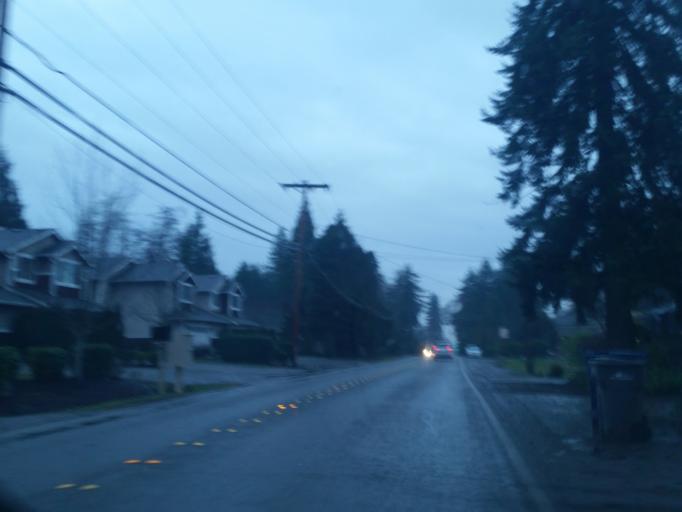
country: US
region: Washington
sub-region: Snohomish County
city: Meadowdale
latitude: 47.8715
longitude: -122.3038
